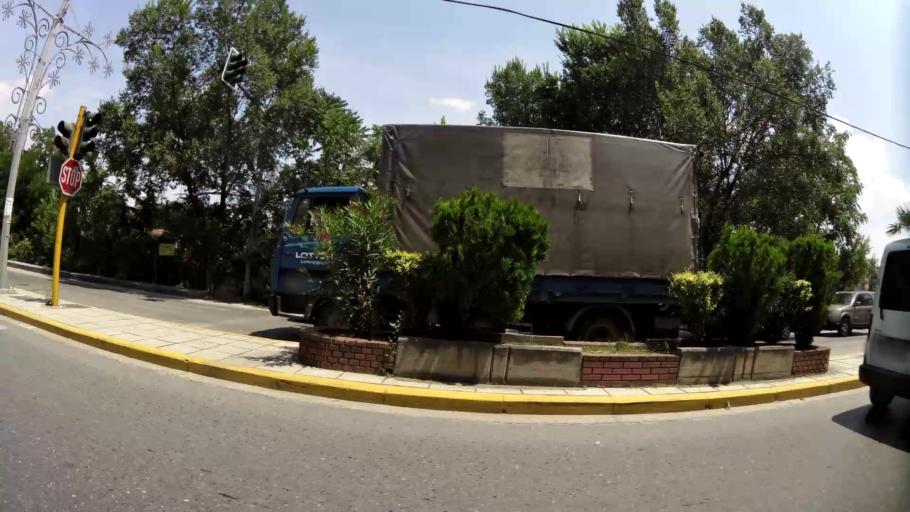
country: GR
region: Central Macedonia
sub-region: Nomos Thessalonikis
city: Ampelokipoi
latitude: 40.6580
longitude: 22.9256
